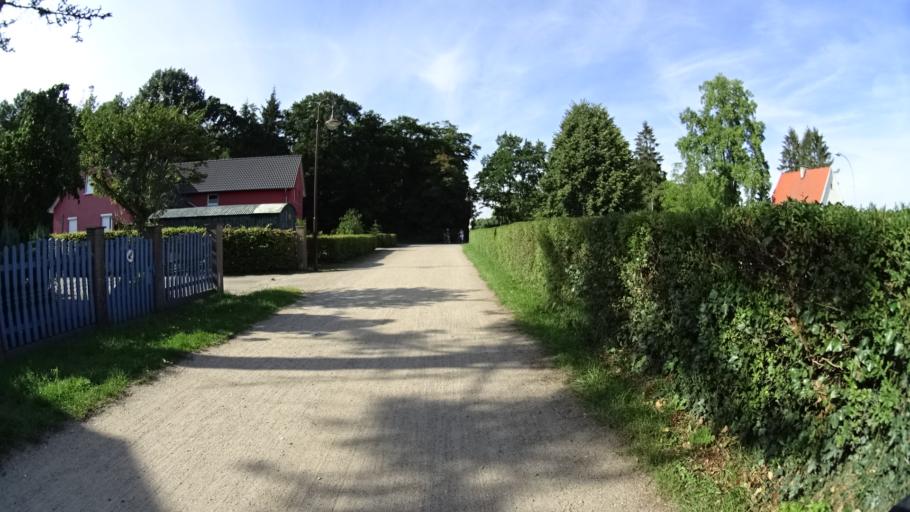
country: DE
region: Lower Saxony
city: Bardowick
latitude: 53.2910
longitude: 10.4007
